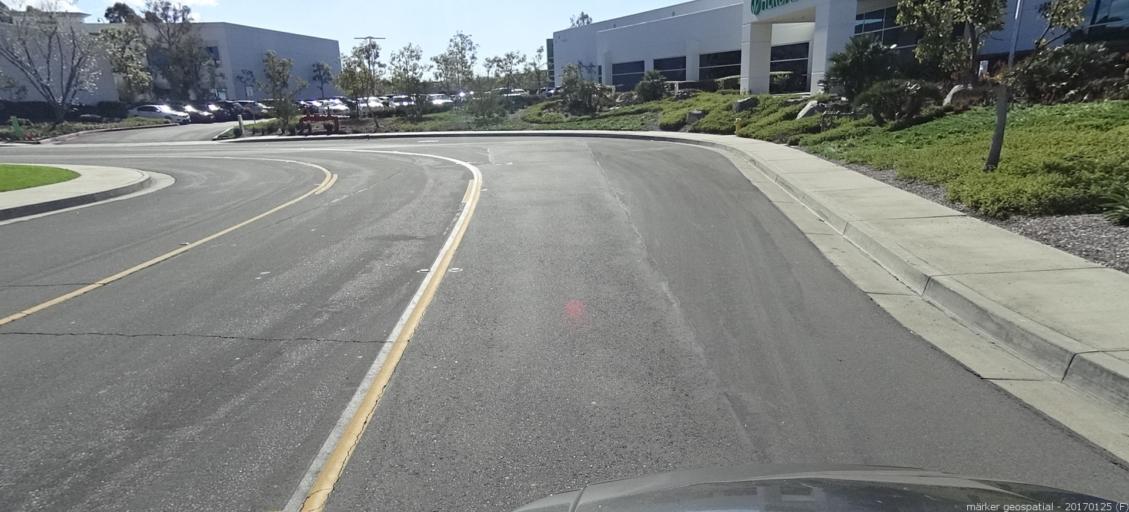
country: US
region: California
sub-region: Orange County
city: Lake Forest
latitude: 33.6653
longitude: -117.6926
